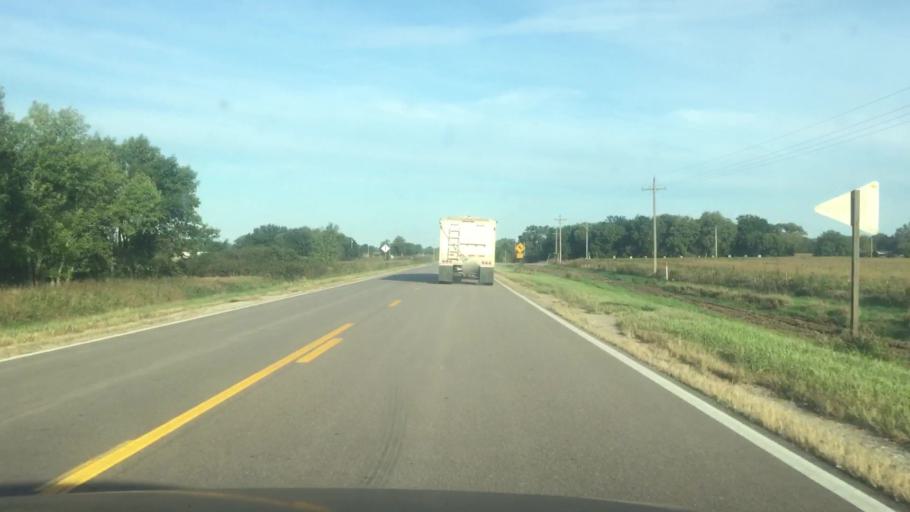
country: US
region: Nebraska
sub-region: Jefferson County
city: Fairbury
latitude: 40.0501
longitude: -97.0286
